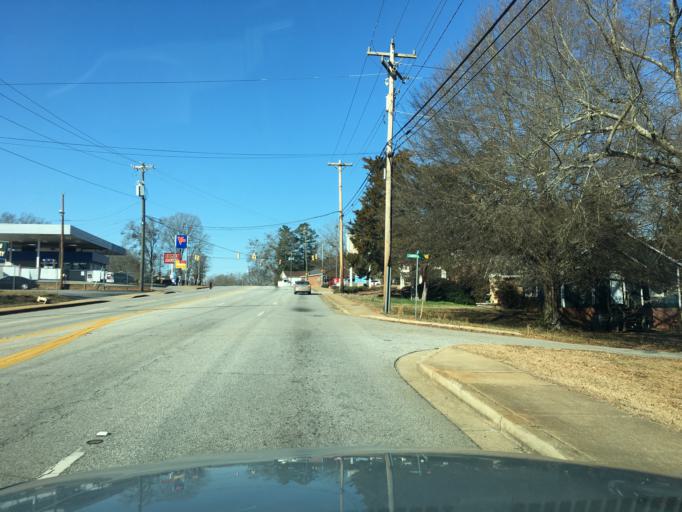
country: US
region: South Carolina
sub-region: Greenville County
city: Sans Souci
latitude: 34.8940
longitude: -82.4305
